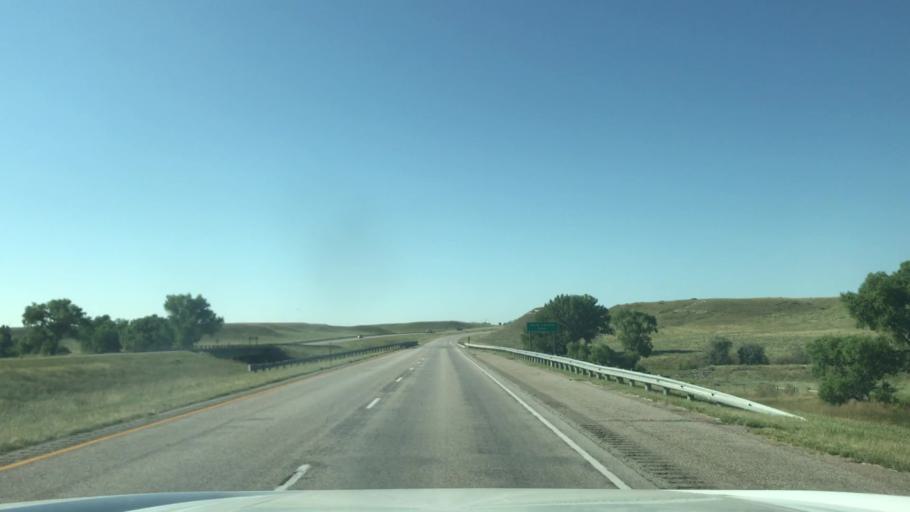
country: US
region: Wyoming
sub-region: Platte County
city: Wheatland
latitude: 42.1578
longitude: -105.0003
